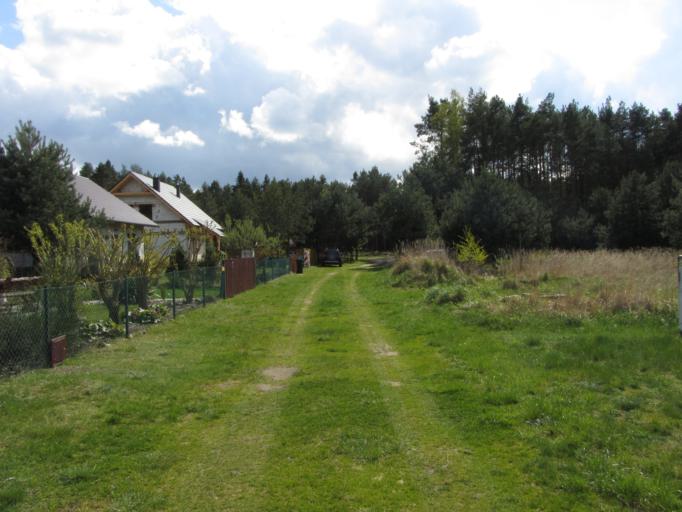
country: PL
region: Lubusz
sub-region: Powiat wschowski
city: Slawa
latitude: 51.8734
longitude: 15.9966
